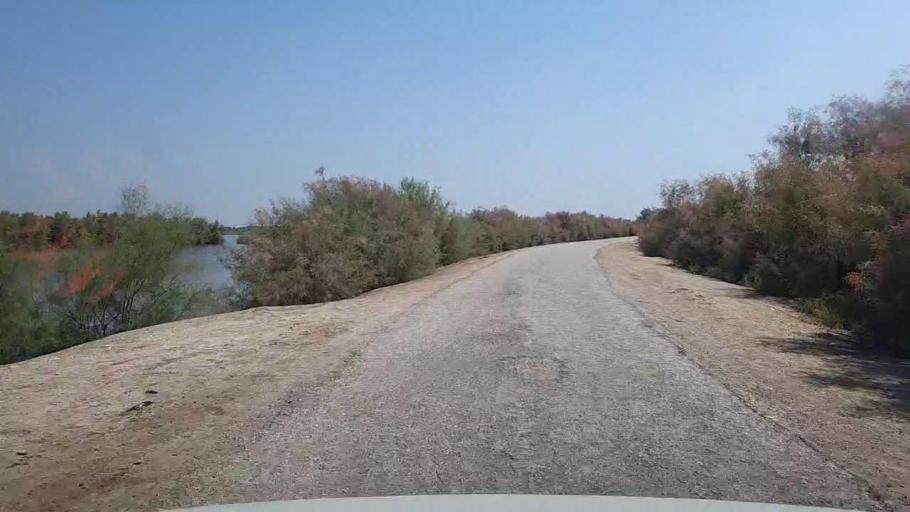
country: PK
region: Sindh
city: Kandhkot
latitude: 28.2996
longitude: 69.3521
